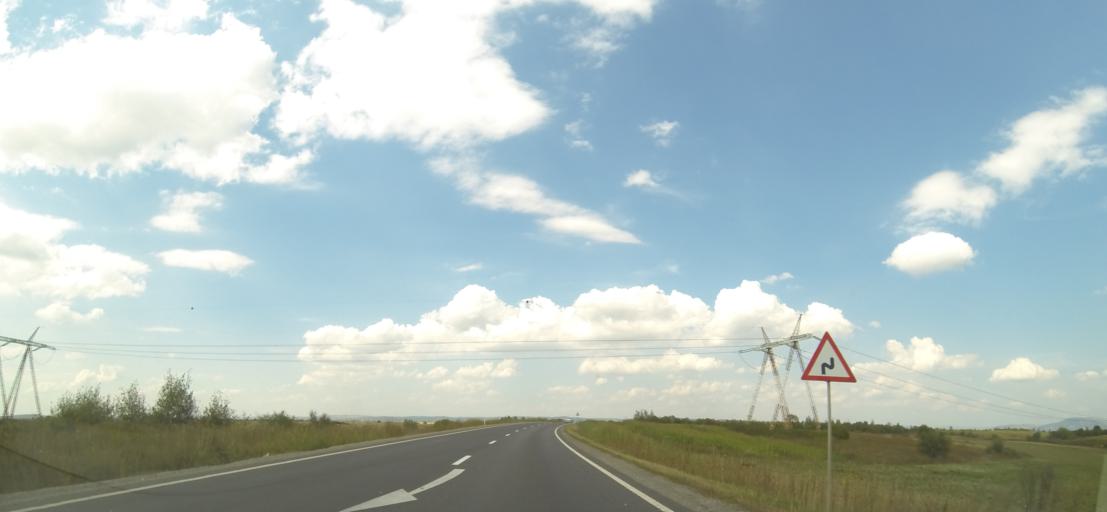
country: RO
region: Brasov
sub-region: Comuna Sinca Veche
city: Sinca Veche
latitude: 45.7961
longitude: 25.1812
